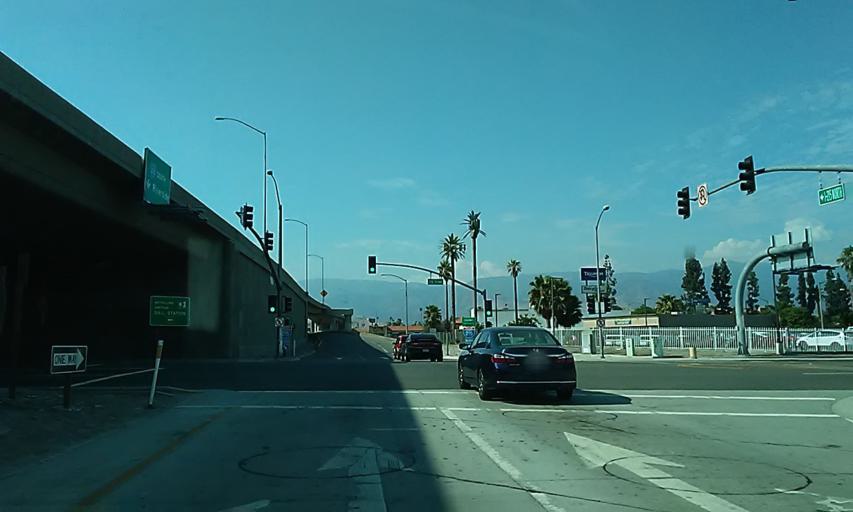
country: US
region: California
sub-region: San Bernardino County
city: San Bernardino
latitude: 34.1043
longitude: -117.3016
